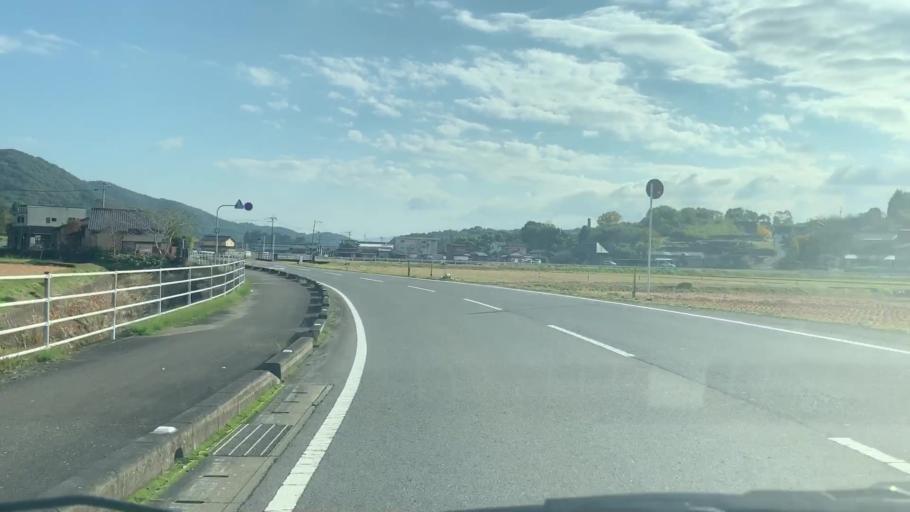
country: JP
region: Saga Prefecture
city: Takeocho-takeo
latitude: 33.1605
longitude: 130.0614
